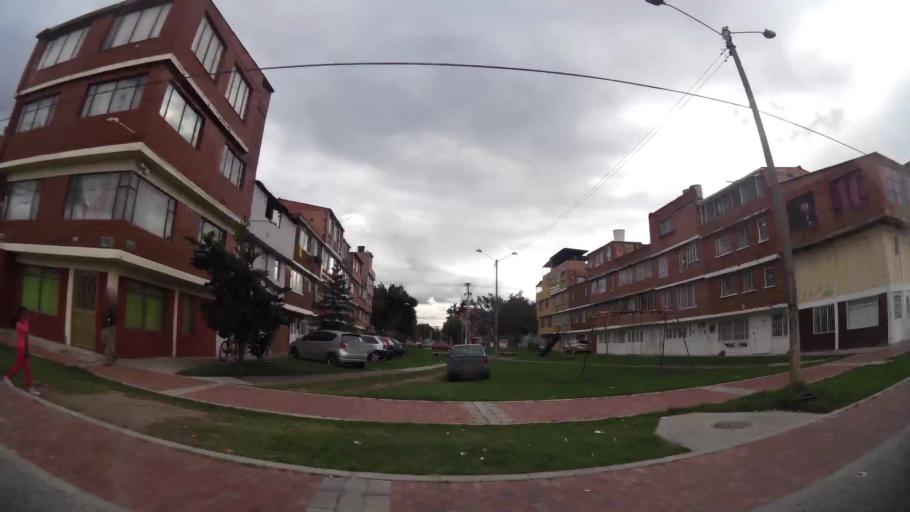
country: CO
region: Cundinamarca
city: Cota
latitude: 4.7173
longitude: -74.1009
